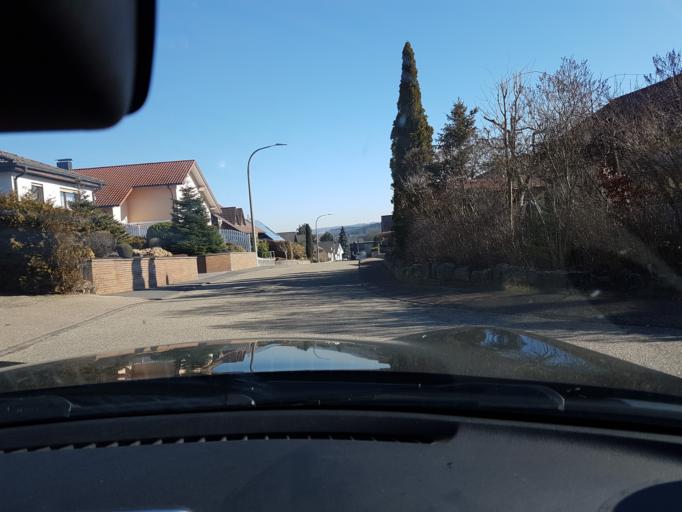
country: DE
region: Baden-Wuerttemberg
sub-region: Karlsruhe Region
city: Osterburken
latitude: 49.4366
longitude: 9.4251
